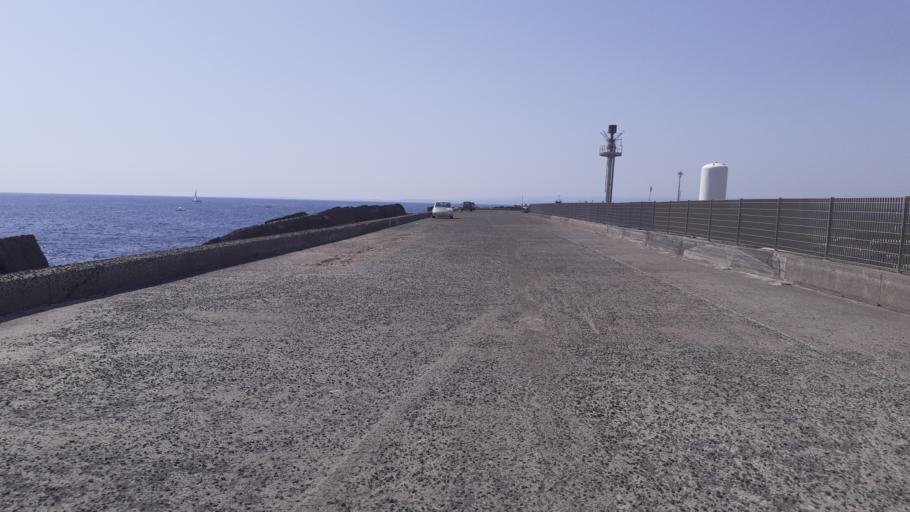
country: IT
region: Sicily
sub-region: Catania
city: Catania
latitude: 37.4926
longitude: 15.0999
